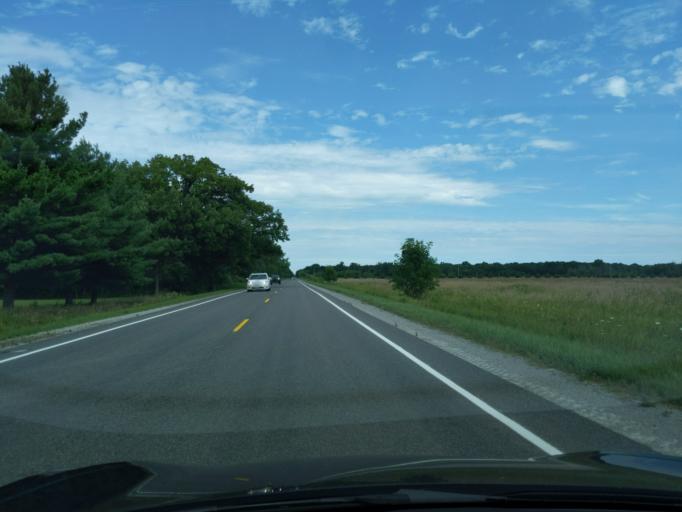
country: US
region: Michigan
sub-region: Gratiot County
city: Breckenridge
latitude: 43.5128
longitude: -84.3698
